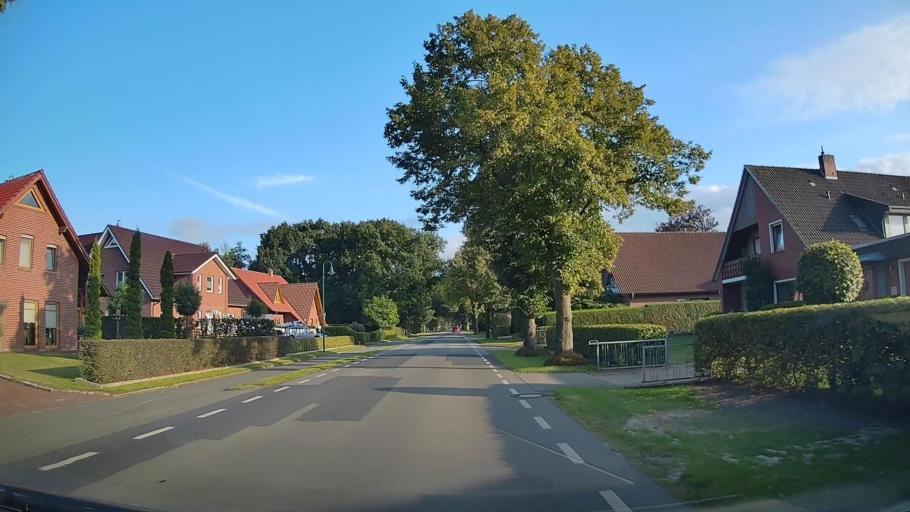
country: DE
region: Lower Saxony
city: Hilkenbrook
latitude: 53.0148
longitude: 7.7589
